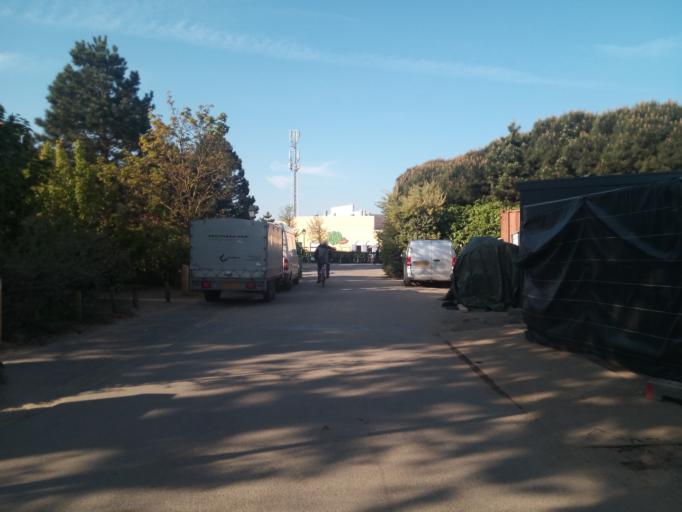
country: NL
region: Zeeland
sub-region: Schouwen-Duiveland
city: Scharendijke
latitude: 51.7558
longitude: 3.8616
